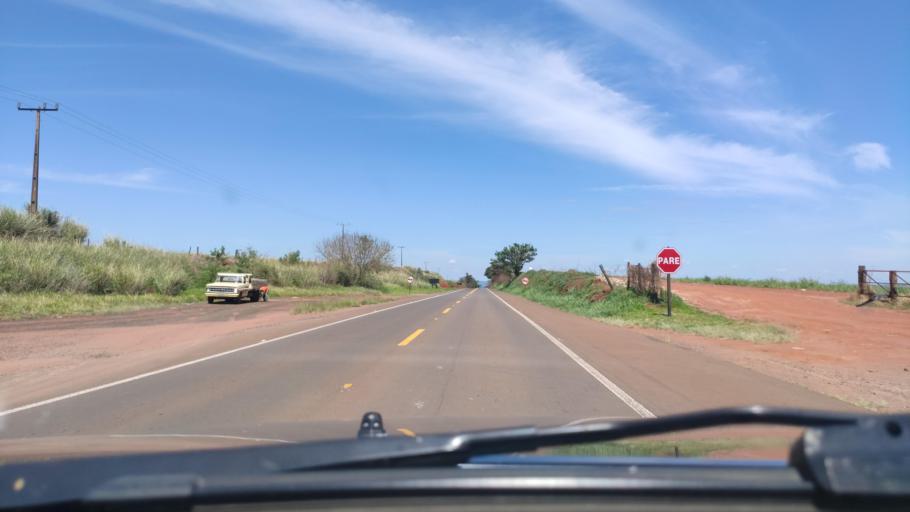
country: BR
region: Sao Paulo
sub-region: Sao Carlos
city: Sao Carlos
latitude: -22.0590
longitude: -47.9827
